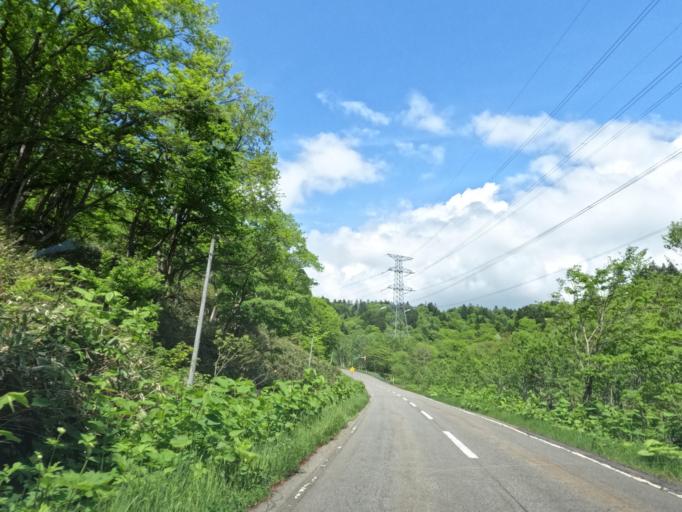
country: JP
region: Hokkaido
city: Takikawa
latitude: 43.5432
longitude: 141.6153
